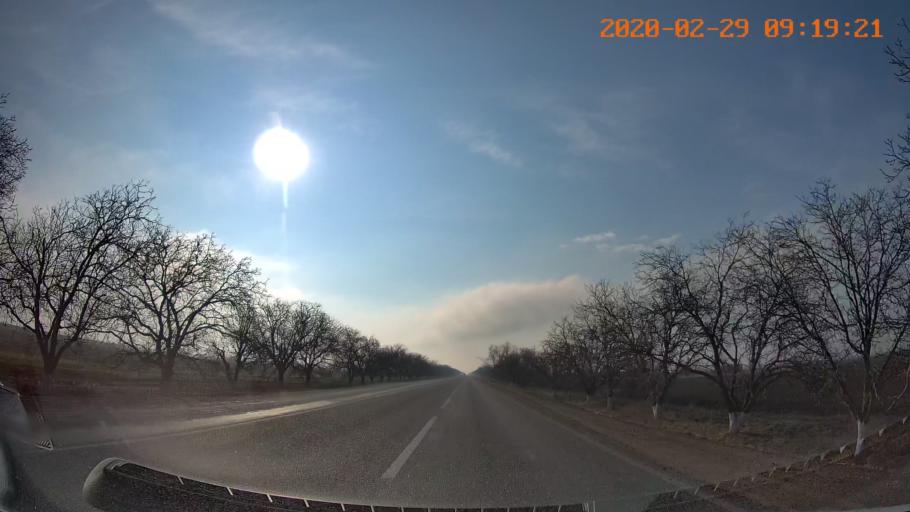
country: MD
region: Telenesti
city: Pervomaisc
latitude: 46.7638
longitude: 29.9383
